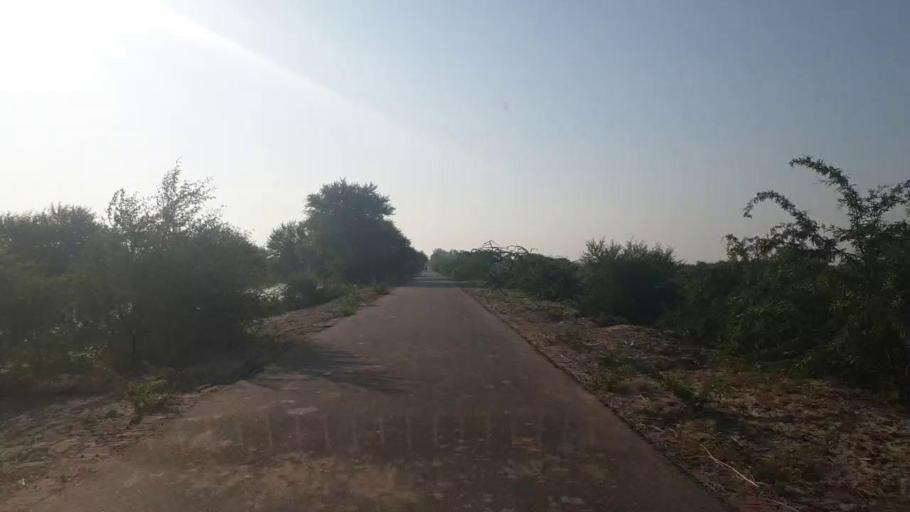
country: PK
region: Sindh
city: Tando Bago
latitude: 24.7303
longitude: 68.9364
